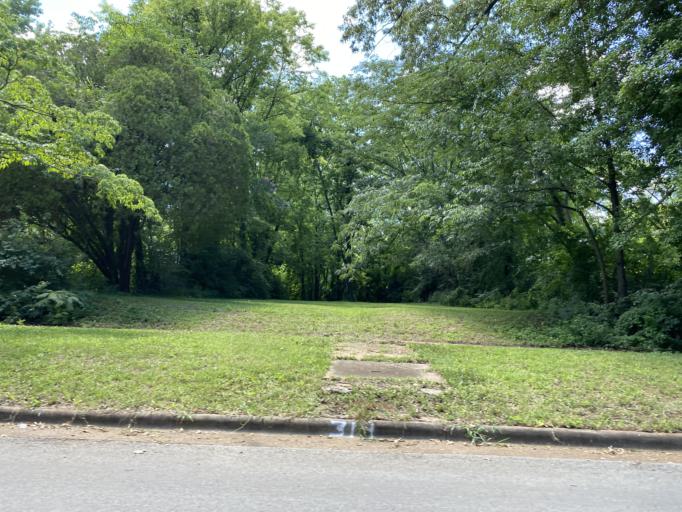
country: US
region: Alabama
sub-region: Morgan County
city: Decatur
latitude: 34.6086
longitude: -86.9925
